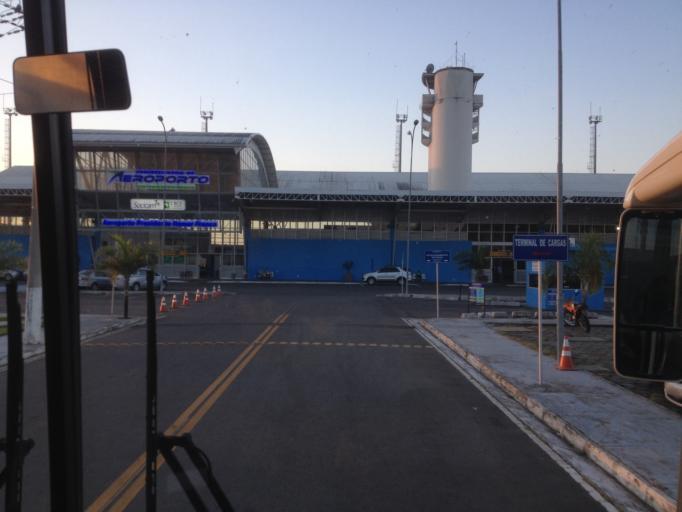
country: BR
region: Minas Gerais
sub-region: Rio Novo
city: Rio Novo
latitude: -21.5109
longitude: -43.1617
